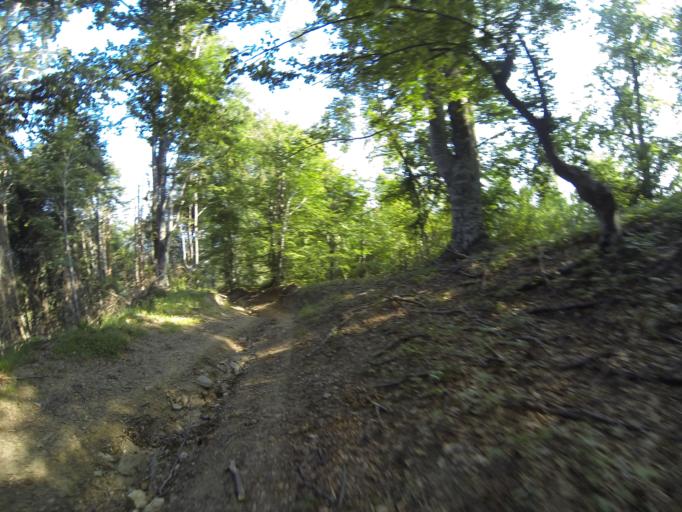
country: RO
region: Valcea
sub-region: Comuna Vaideeni
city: Vaideeni
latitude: 45.2156
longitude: 23.9725
